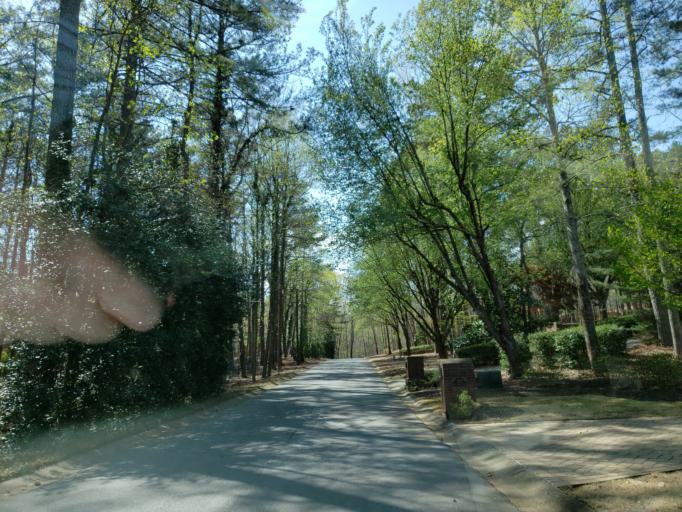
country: US
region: Georgia
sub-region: Cobb County
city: Marietta
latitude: 33.9706
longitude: -84.5669
